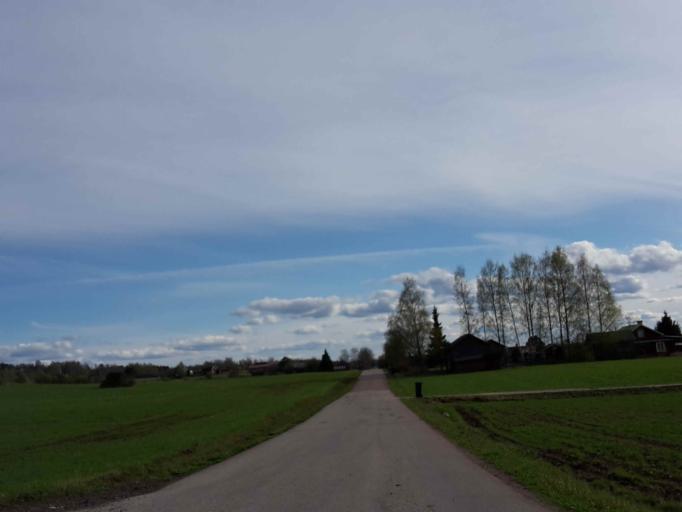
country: SE
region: Dalarna
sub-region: Orsa Kommun
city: Orsa
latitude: 61.0954
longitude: 14.6201
